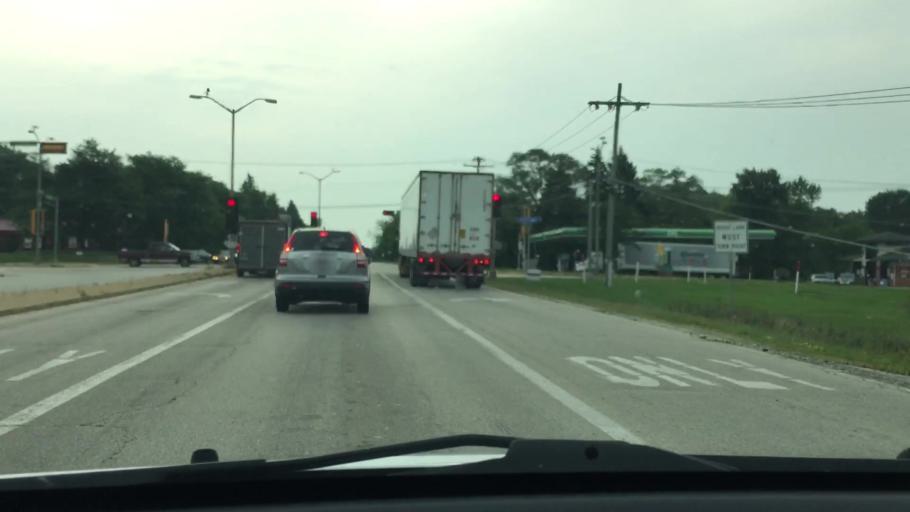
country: US
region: Wisconsin
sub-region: Waukesha County
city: New Berlin
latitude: 42.9954
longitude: -88.1092
